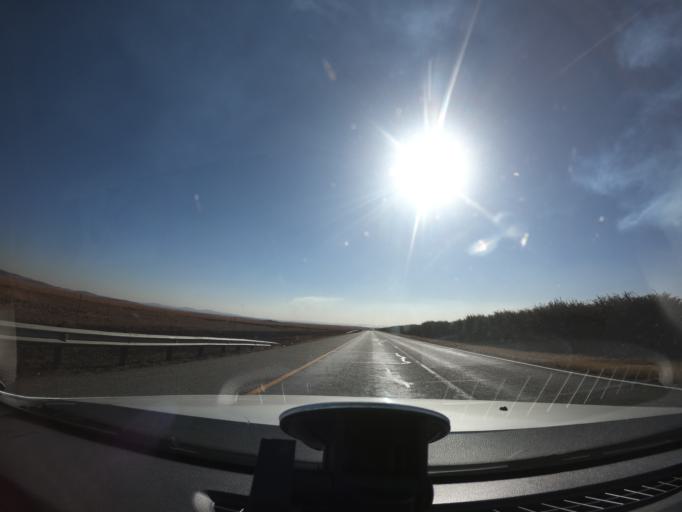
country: ZA
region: Gauteng
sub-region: Sedibeng District Municipality
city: Heidelberg
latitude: -26.4353
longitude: 28.2999
